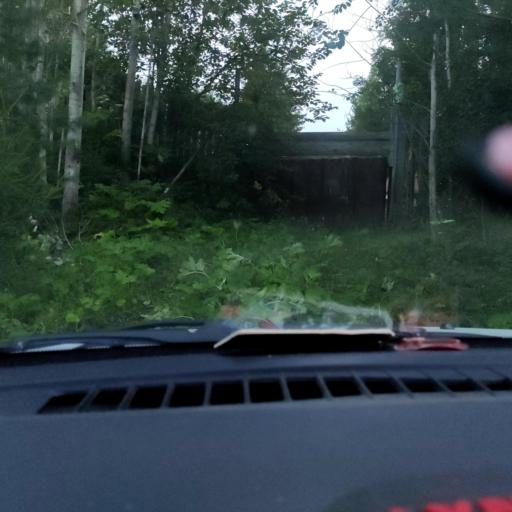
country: RU
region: Perm
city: Kultayevo
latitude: 57.8209
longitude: 55.9991
